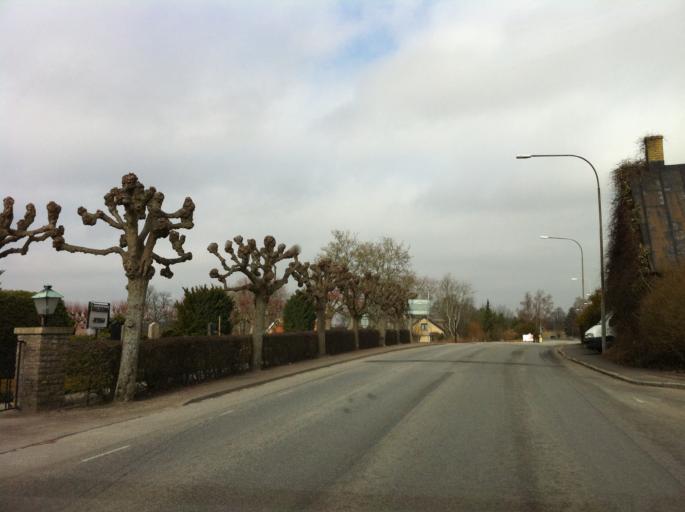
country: SE
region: Skane
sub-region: Lunds Kommun
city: Lund
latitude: 55.7360
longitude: 13.1749
